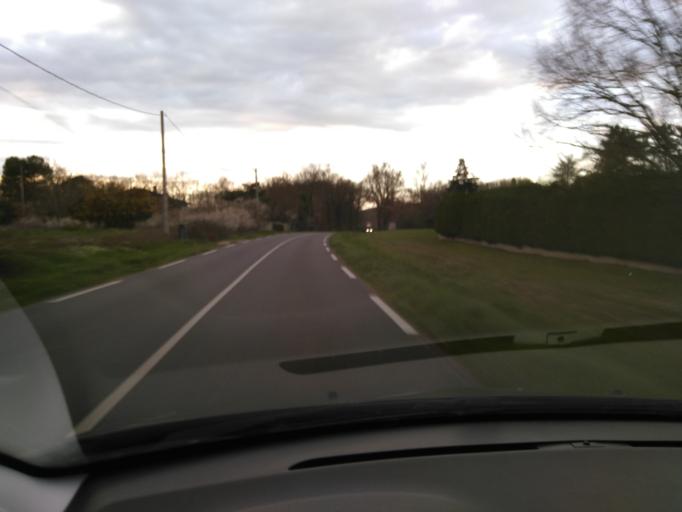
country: FR
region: Midi-Pyrenees
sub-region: Departement de la Haute-Garonne
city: Brax
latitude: 43.6133
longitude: 1.2611
